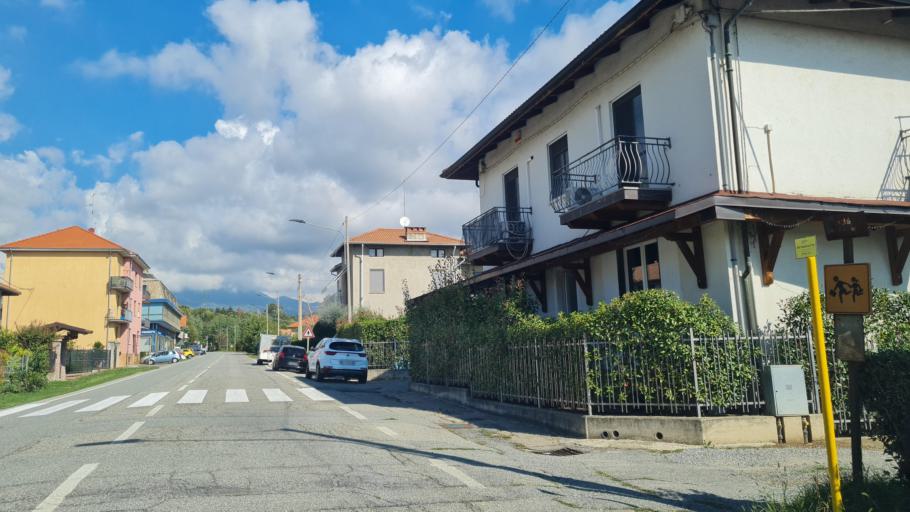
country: IT
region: Piedmont
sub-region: Provincia di Biella
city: Lessona
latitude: 45.5890
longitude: 8.1851
